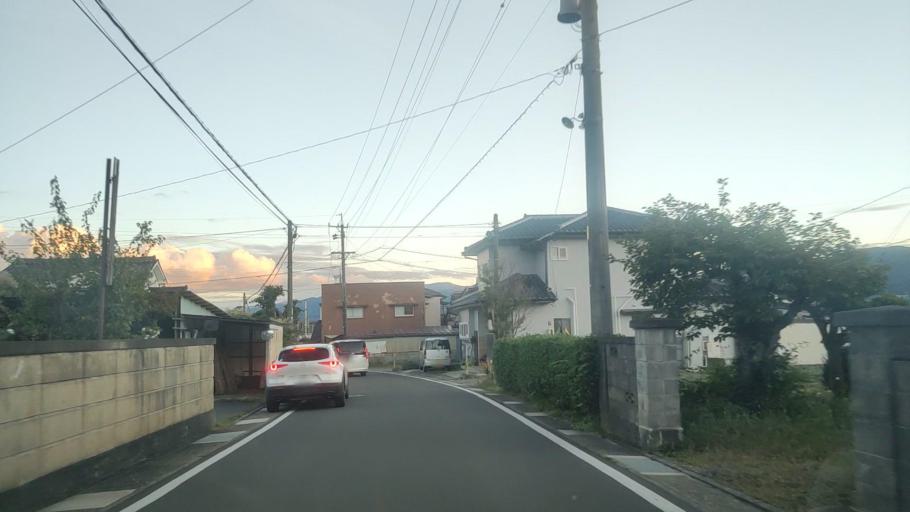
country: JP
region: Nagano
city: Okaya
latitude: 36.0701
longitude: 138.0550
